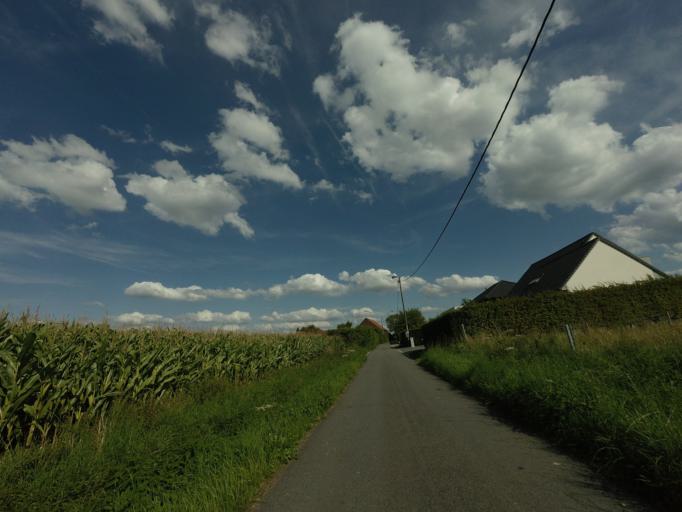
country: BE
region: Flanders
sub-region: Provincie Vlaams-Brabant
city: Meise
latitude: 50.9500
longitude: 4.3421
